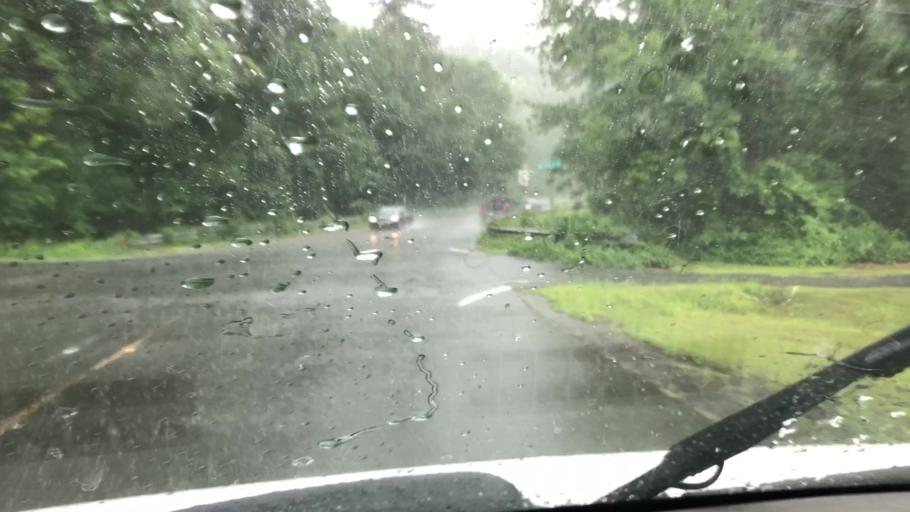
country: US
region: Massachusetts
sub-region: Hampshire County
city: Williamsburg
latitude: 42.4028
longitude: -72.7463
